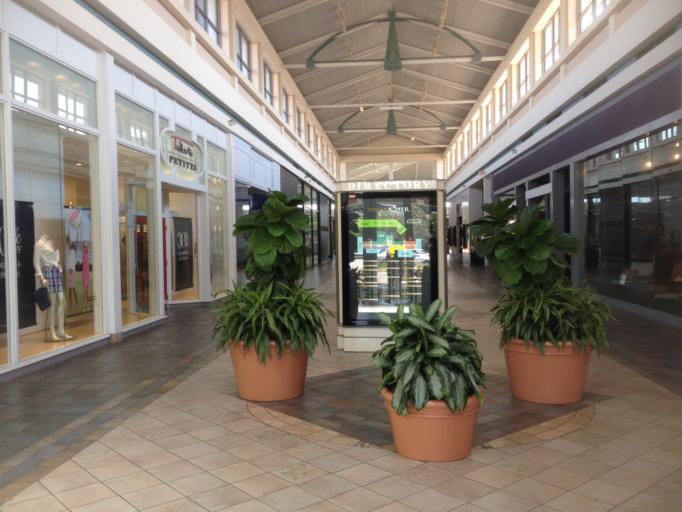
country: US
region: Florida
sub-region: Indian River County
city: West Vero Corridor
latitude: 27.6419
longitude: -80.4590
